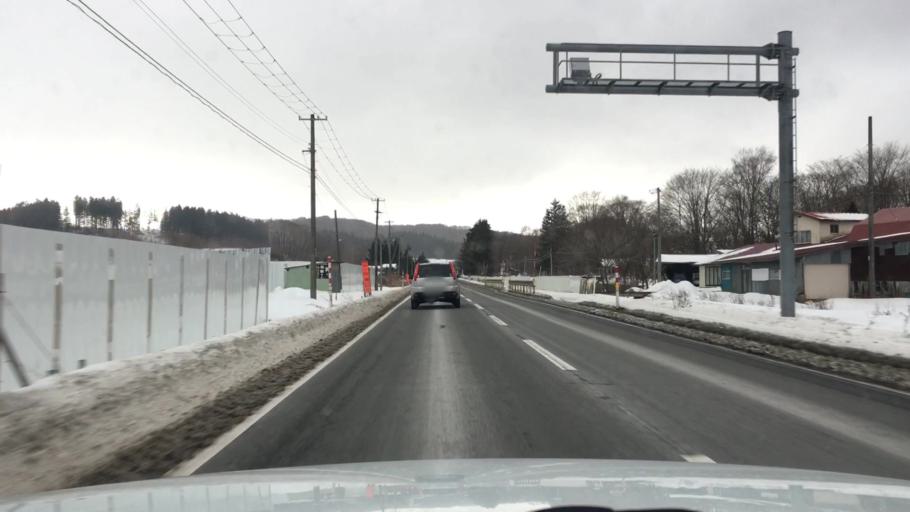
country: JP
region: Iwate
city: Morioka-shi
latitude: 39.6461
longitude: 141.3649
